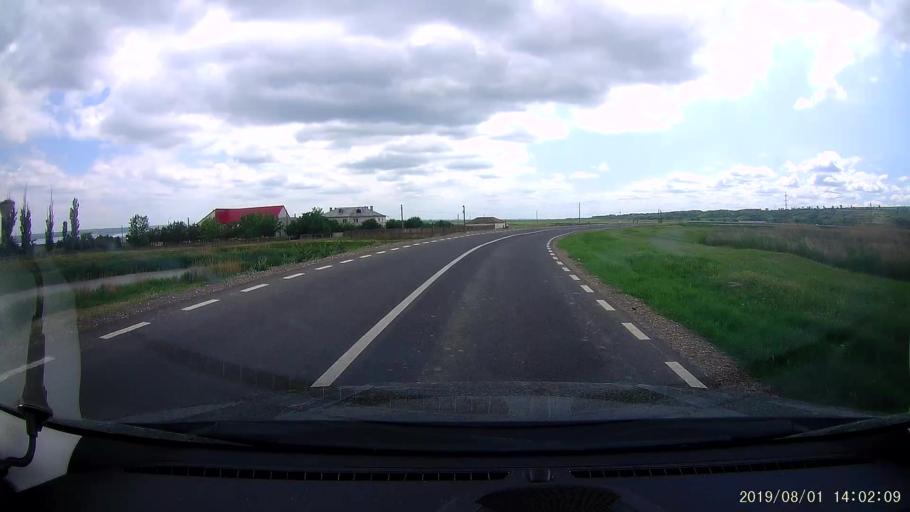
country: RO
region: Galati
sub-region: Comuna Foltesti
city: Foltesti
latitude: 45.7389
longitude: 28.0784
